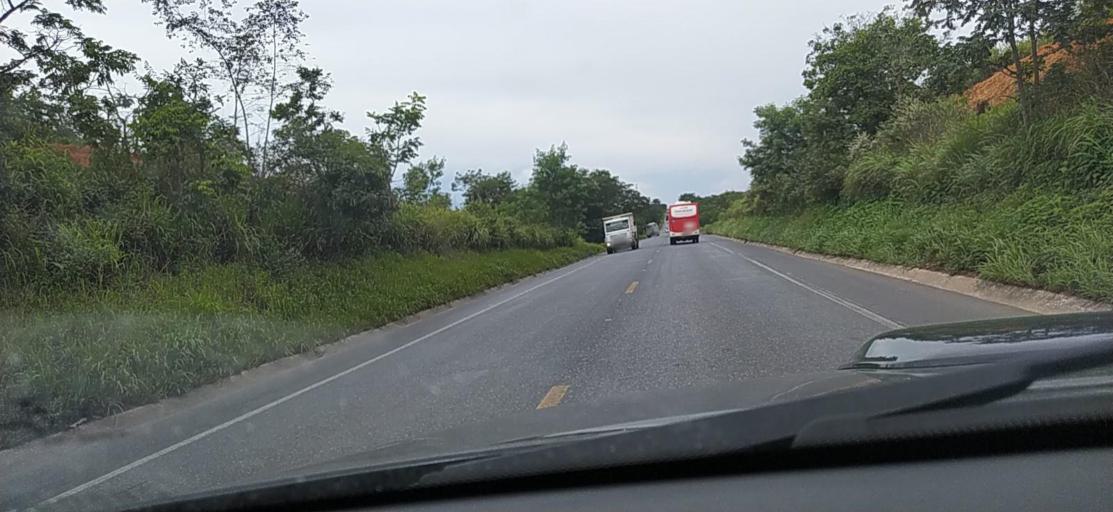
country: BR
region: Minas Gerais
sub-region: Montes Claros
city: Montes Claros
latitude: -16.6638
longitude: -43.7791
